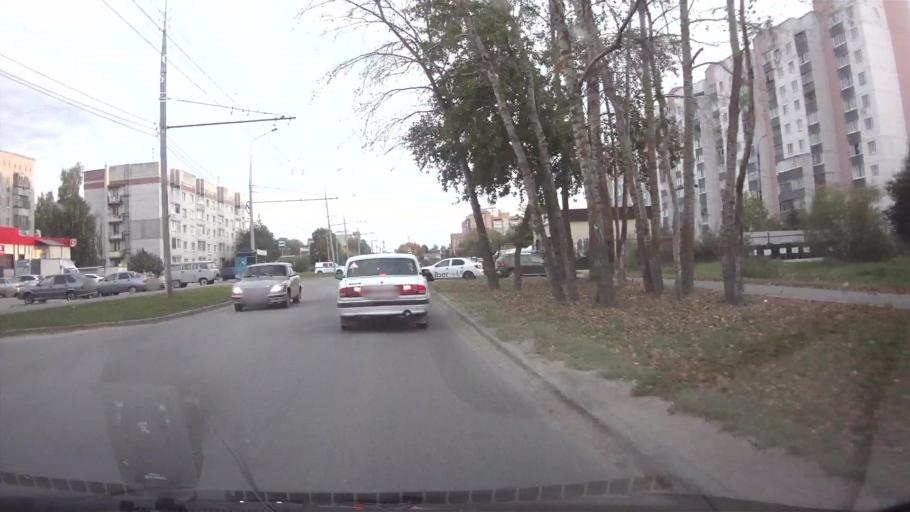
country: RU
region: Mariy-El
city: Yoshkar-Ola
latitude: 56.6508
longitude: 47.8550
